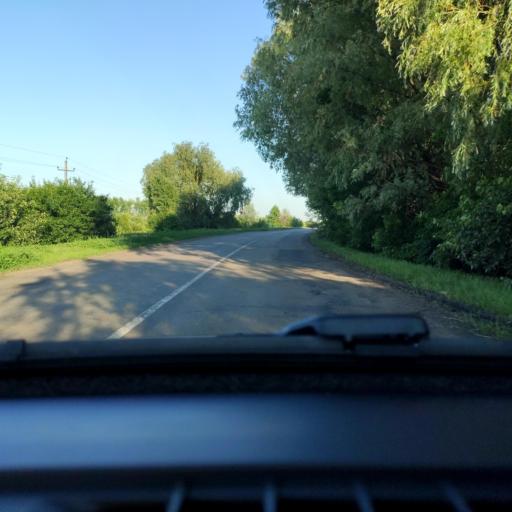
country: RU
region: Voronezj
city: Kashirskoye
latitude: 51.4905
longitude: 39.8492
